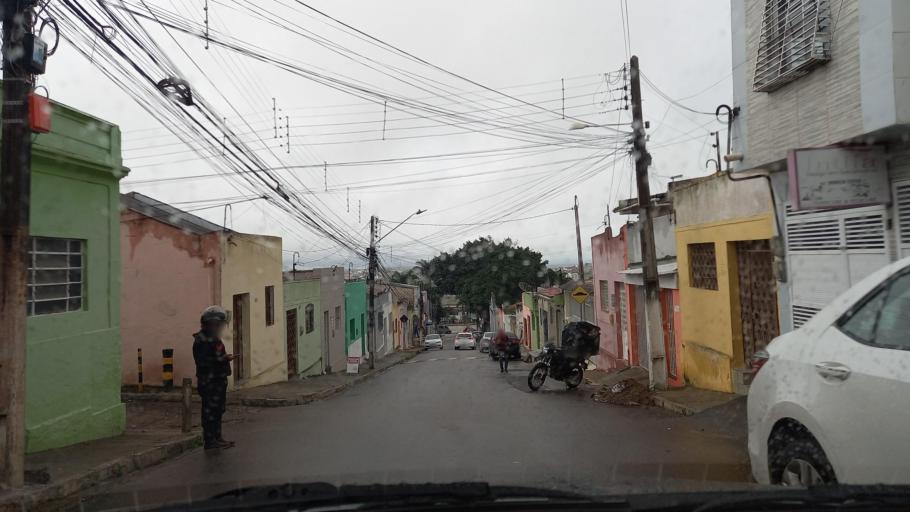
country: BR
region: Pernambuco
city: Garanhuns
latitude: -8.8867
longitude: -36.4934
